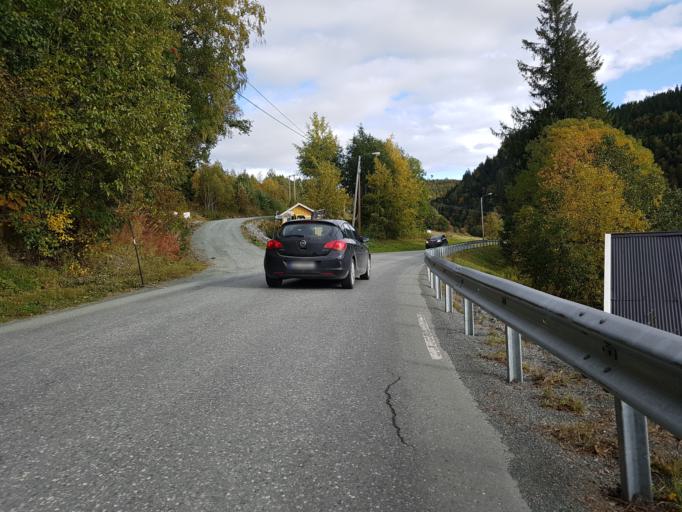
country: NO
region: Sor-Trondelag
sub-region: Klaebu
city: Klaebu
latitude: 63.3979
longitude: 10.5505
